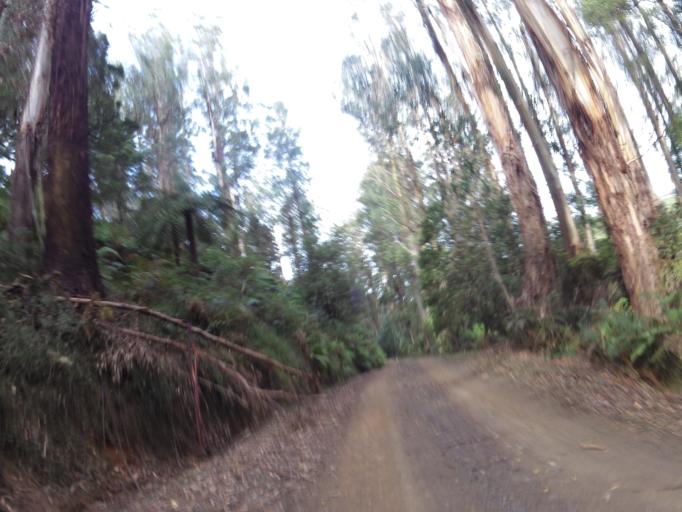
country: AU
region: Victoria
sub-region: Baw Baw
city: Warragul
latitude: -37.8968
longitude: 145.9739
